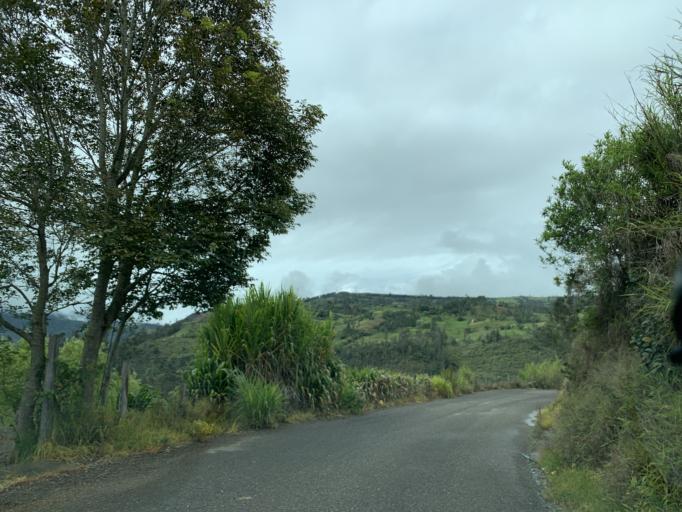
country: CO
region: Boyaca
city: Tibana
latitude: 5.3123
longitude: -73.4155
